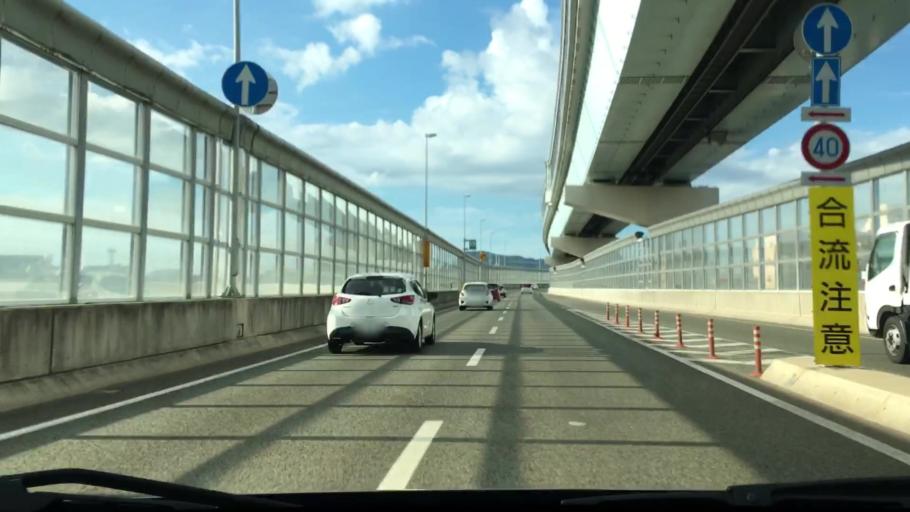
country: JP
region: Fukuoka
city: Fukuoka-shi
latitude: 33.5745
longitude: 130.3161
